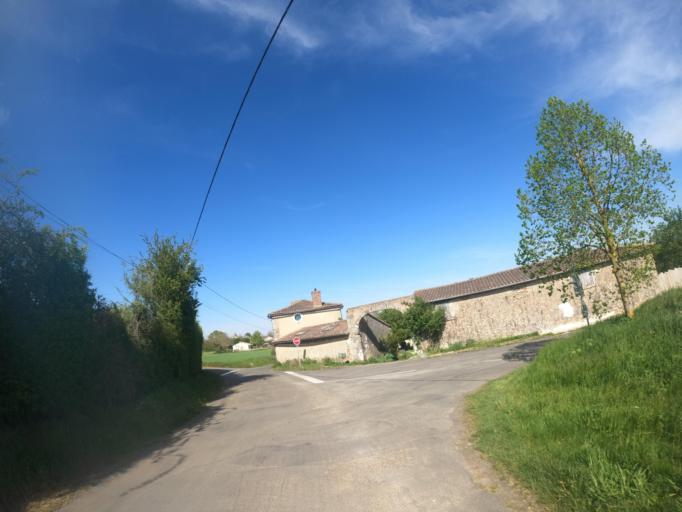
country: FR
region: Poitou-Charentes
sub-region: Departement des Deux-Sevres
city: Saint-Varent
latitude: 46.9073
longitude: -0.2159
